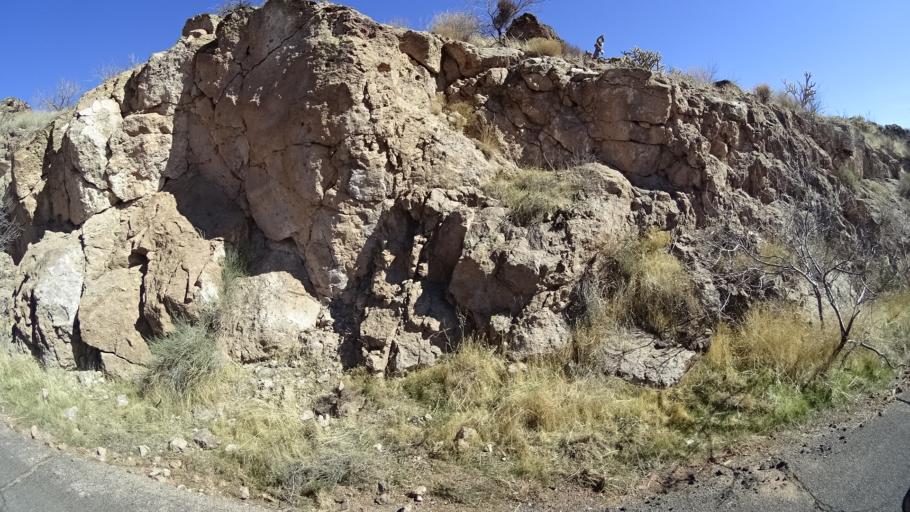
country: US
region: Arizona
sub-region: Mohave County
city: Kingman
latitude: 35.1892
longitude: -114.0382
